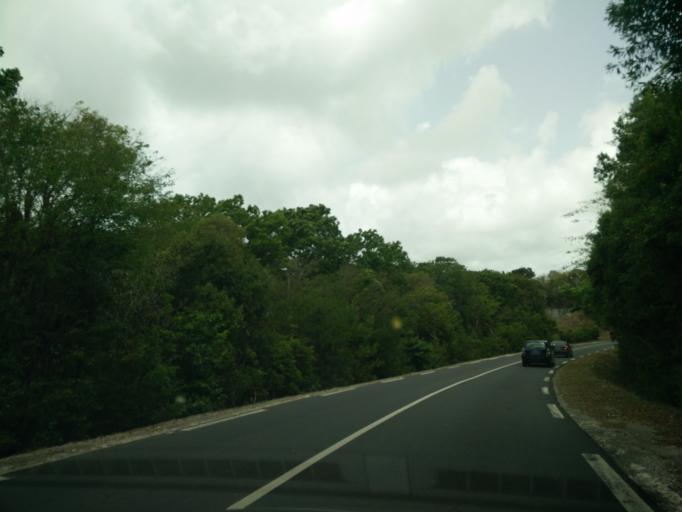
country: GP
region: Guadeloupe
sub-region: Guadeloupe
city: Petit-Canal
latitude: 16.3718
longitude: -61.4684
